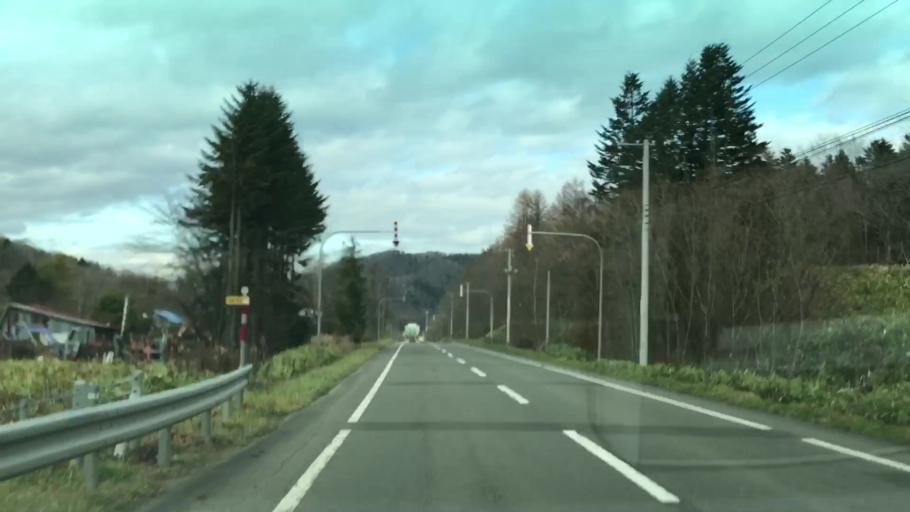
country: JP
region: Hokkaido
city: Shimo-furano
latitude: 42.9399
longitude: 142.4447
